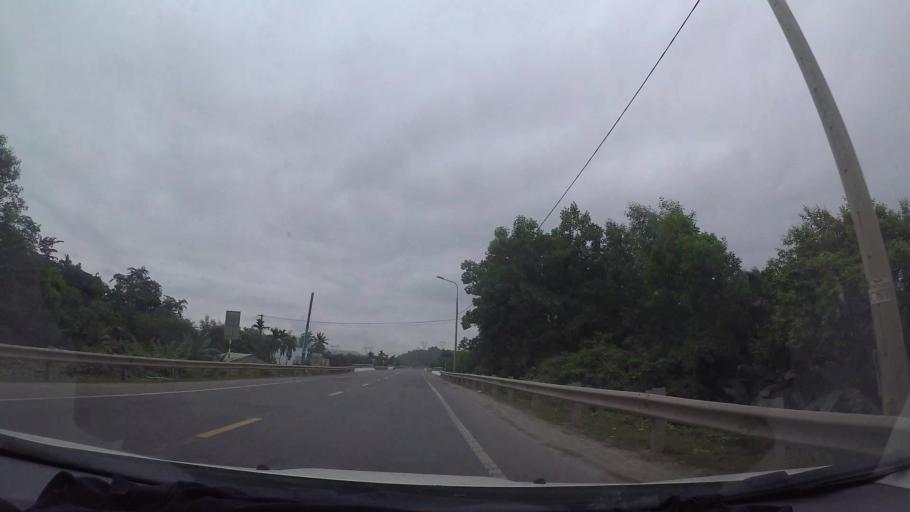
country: VN
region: Da Nang
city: Lien Chieu
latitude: 16.0785
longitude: 108.0858
